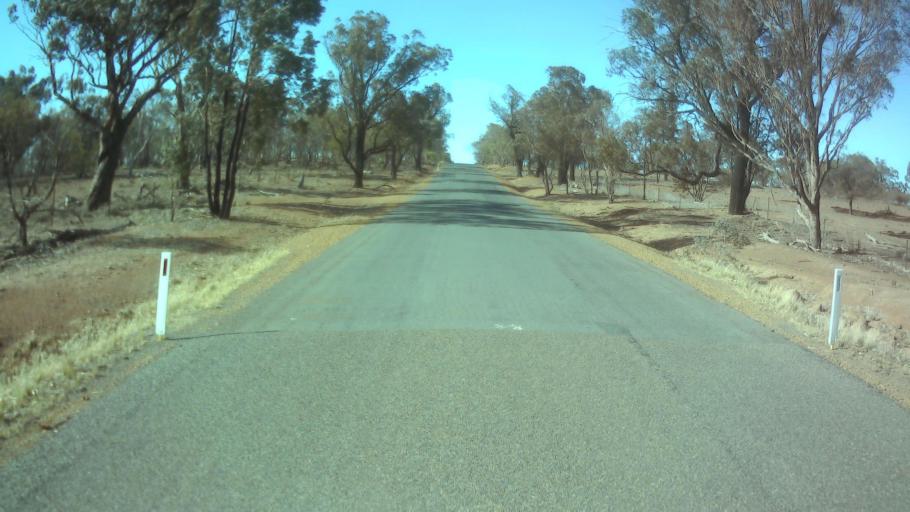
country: AU
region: New South Wales
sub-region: Forbes
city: Forbes
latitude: -33.7068
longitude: 147.8055
